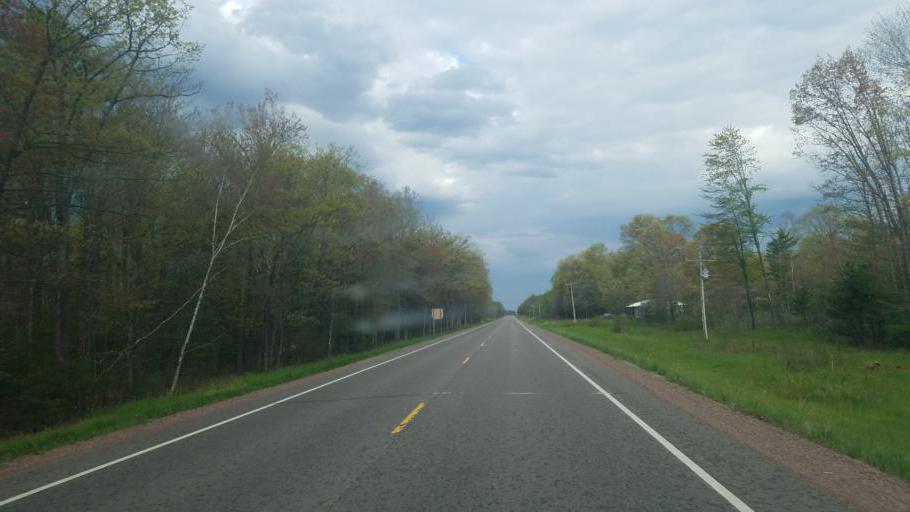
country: US
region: Wisconsin
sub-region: Wood County
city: Nekoosa
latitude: 44.3802
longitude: -90.1462
